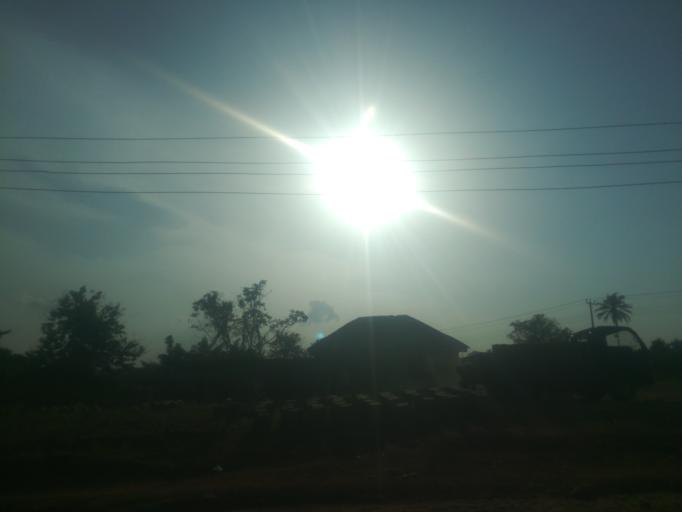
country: NG
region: Oyo
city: Moniya
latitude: 7.5555
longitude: 3.8890
